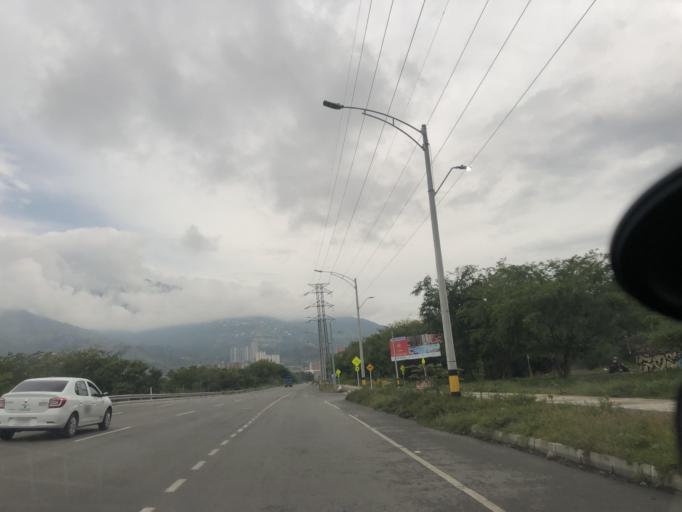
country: CO
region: Antioquia
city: Bello
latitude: 6.3262
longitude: -75.5519
